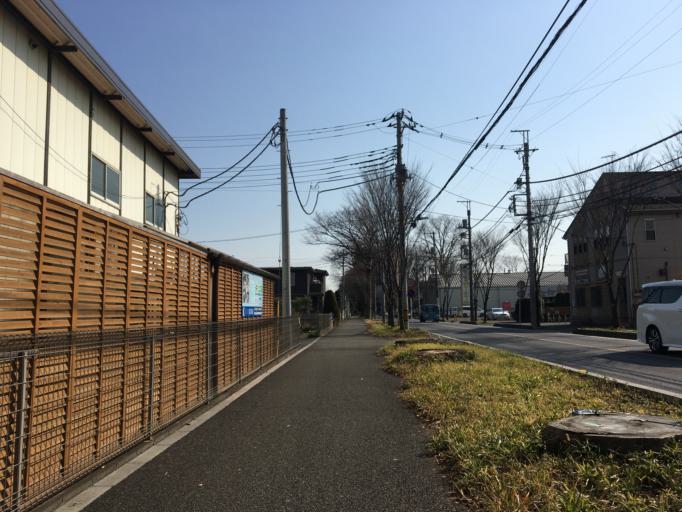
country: JP
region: Saitama
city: Oi
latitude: 35.8263
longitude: 139.5071
